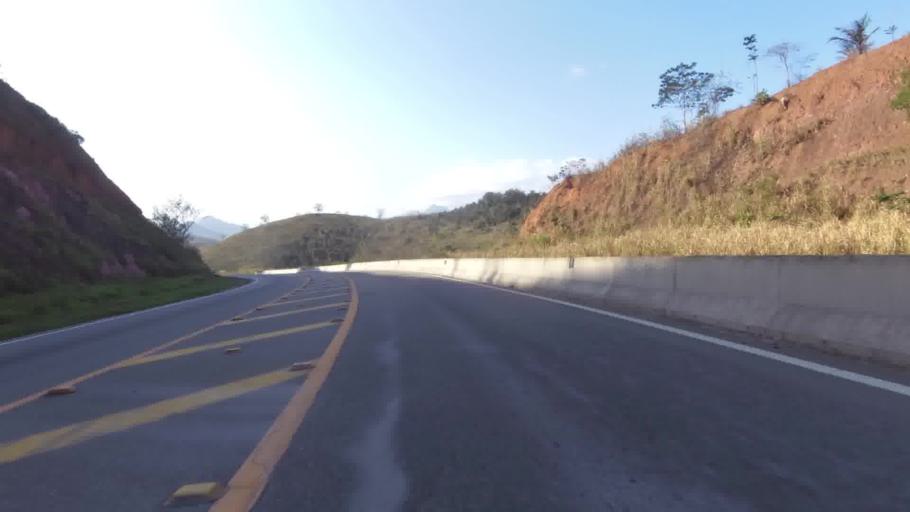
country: BR
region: Espirito Santo
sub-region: Mimoso Do Sul
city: Mimoso do Sul
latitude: -21.2083
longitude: -41.2985
